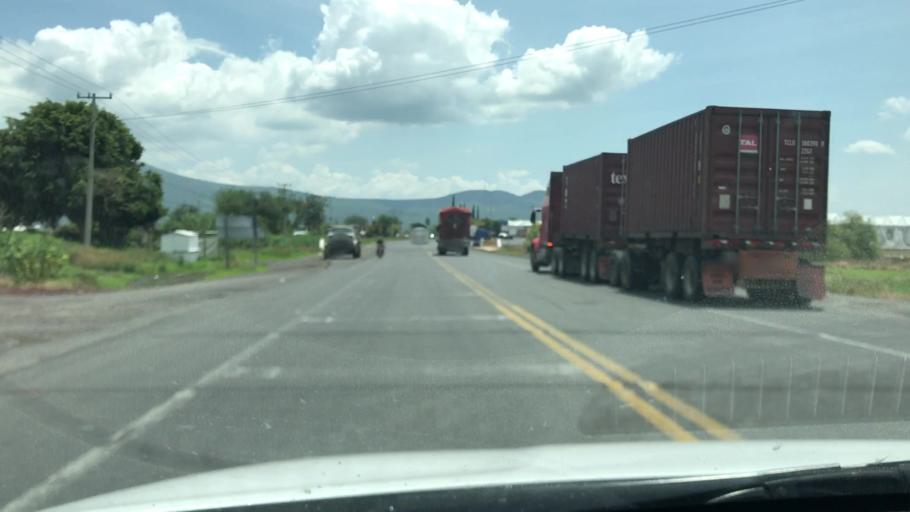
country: MX
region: Michoacan
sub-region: Yurecuaro
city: Yurecuaro
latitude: 20.3179
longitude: -102.3037
